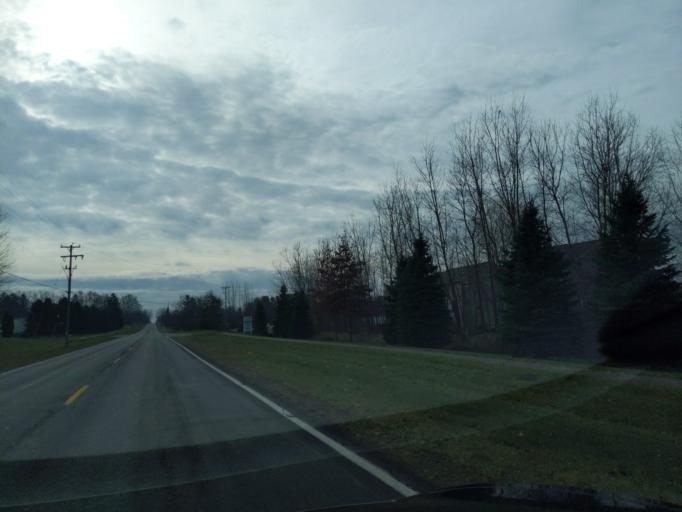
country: US
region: Michigan
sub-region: Ingham County
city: Holt
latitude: 42.6241
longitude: -84.5232
